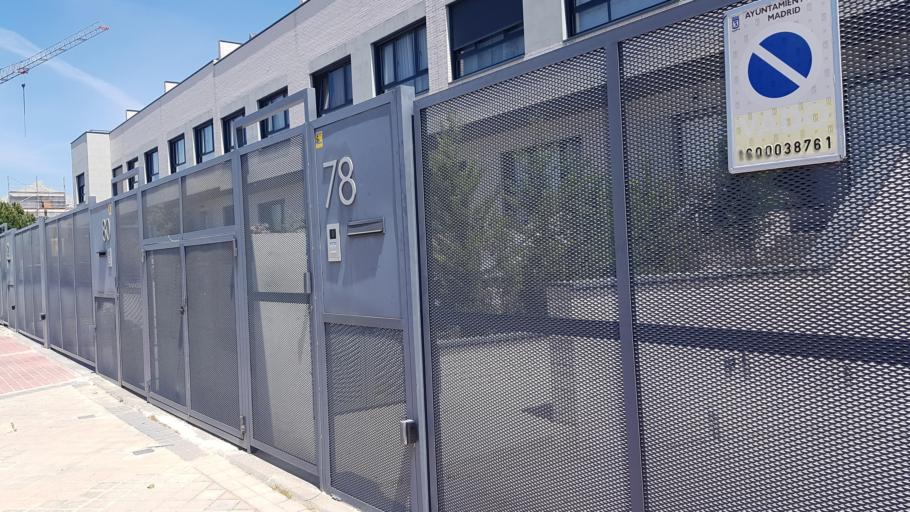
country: ES
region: Madrid
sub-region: Provincia de Madrid
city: Hortaleza
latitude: 40.4814
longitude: -3.6365
